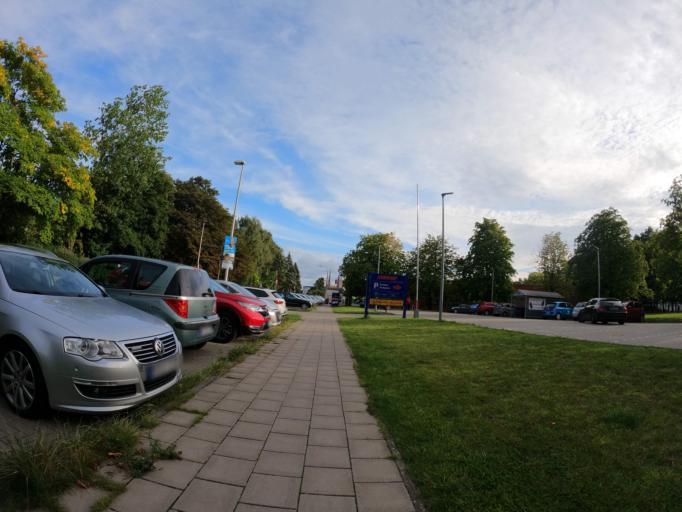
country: DE
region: Mecklenburg-Vorpommern
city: Kramerhof
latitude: 54.3297
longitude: 13.0546
